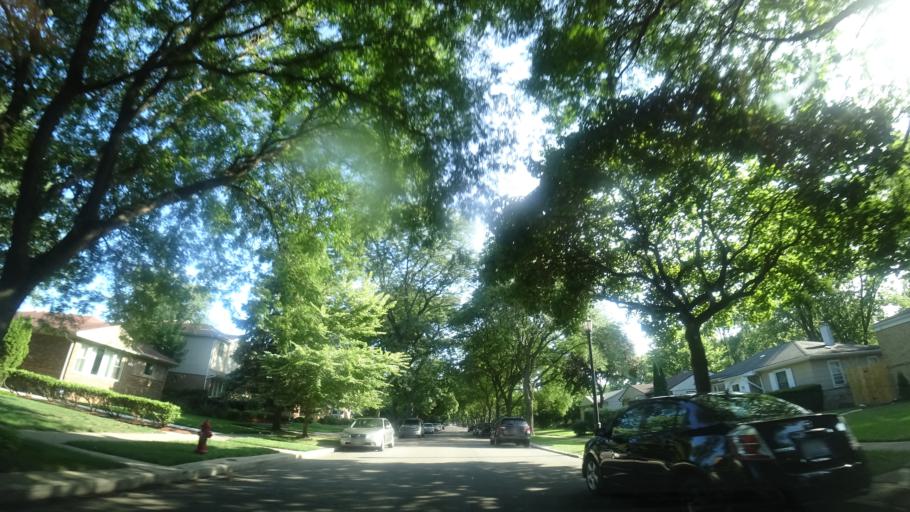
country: US
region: Illinois
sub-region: Cook County
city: Evanston
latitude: 42.0387
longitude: -87.7070
